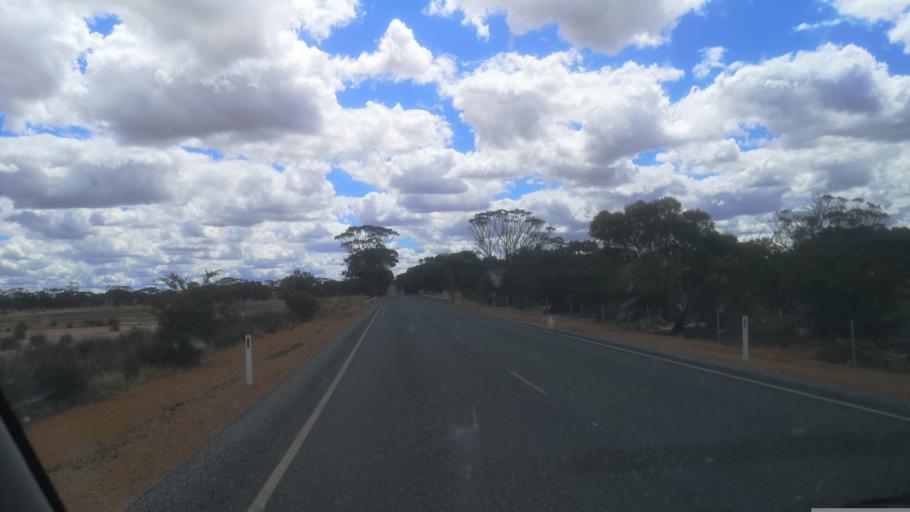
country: AU
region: Western Australia
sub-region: Beverley
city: Beverley
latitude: -31.9899
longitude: 117.1268
